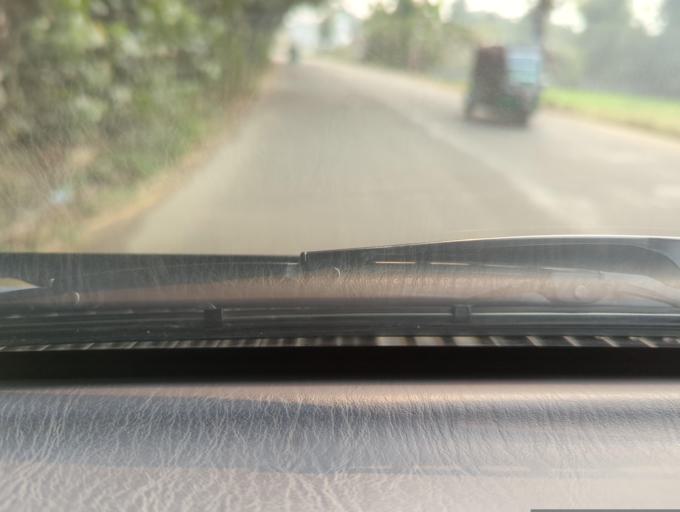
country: BD
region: Sylhet
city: Maulavi Bazar
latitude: 24.5000
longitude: 91.7354
